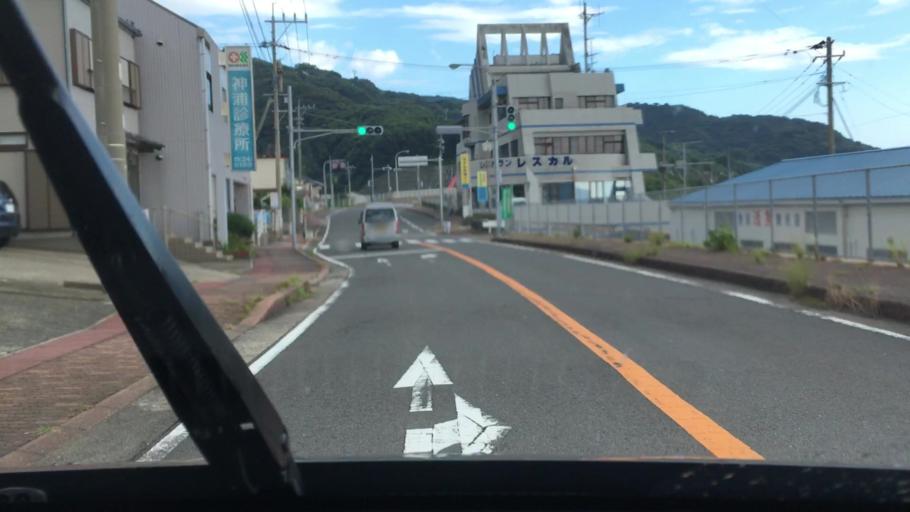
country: JP
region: Nagasaki
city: Togitsu
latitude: 32.8812
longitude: 129.6795
